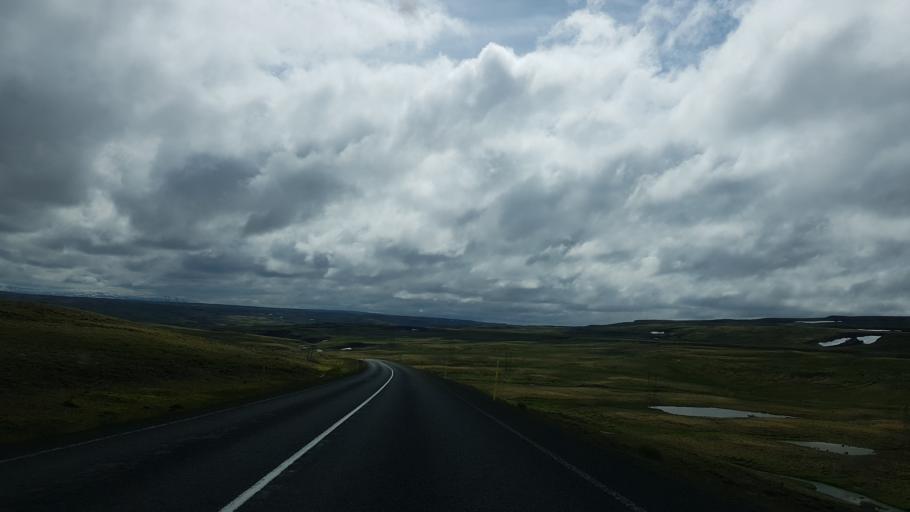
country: IS
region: West
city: Borgarnes
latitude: 64.9744
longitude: -21.0669
